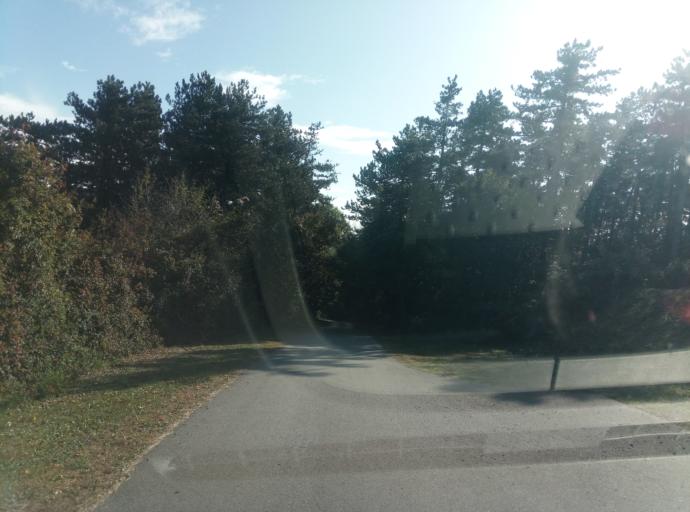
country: SI
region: Ajdovscina
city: Lokavec
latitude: 45.8200
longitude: 13.8518
